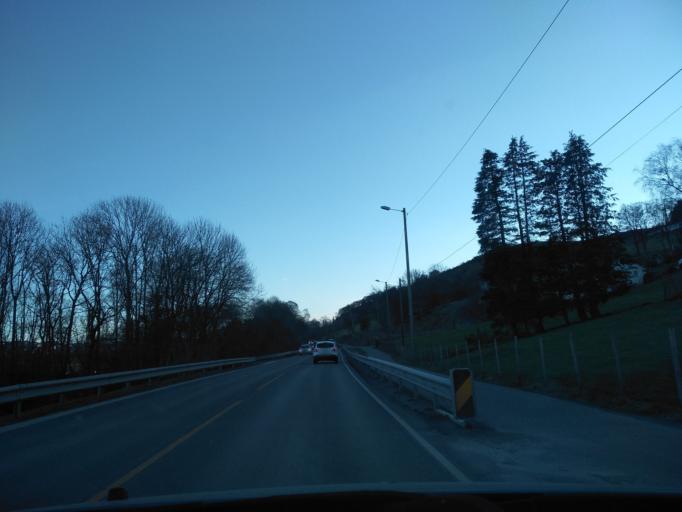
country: NO
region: Rogaland
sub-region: Tysvaer
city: Aksdal
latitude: 59.4370
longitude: 5.4607
